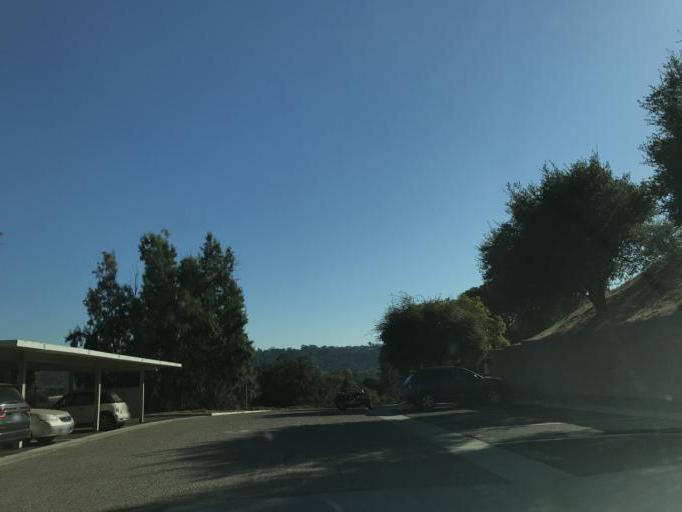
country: US
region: California
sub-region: Santa Barbara County
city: Goleta
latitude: 34.4480
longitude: -119.7812
